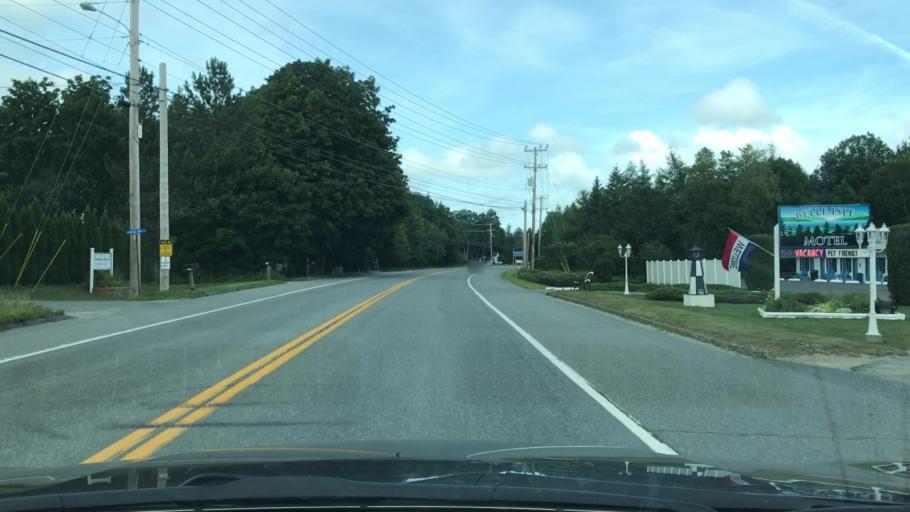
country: US
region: Maine
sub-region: Hancock County
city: Trenton
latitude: 44.4343
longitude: -68.3172
